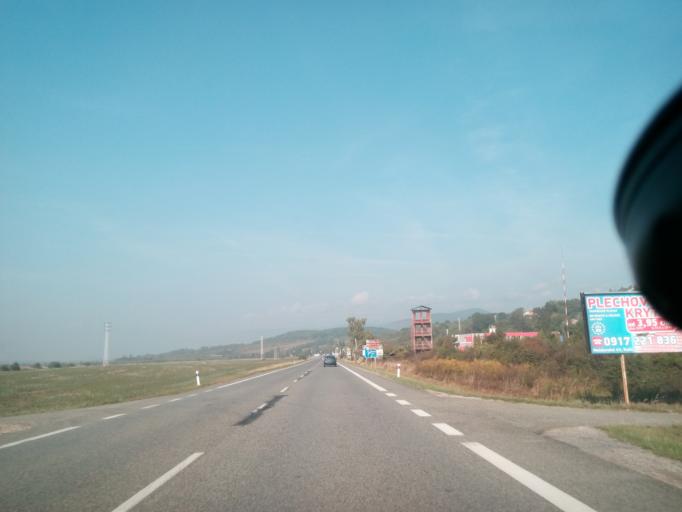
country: SK
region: Kosicky
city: Moldava nad Bodvou
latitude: 48.6072
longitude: 20.9931
